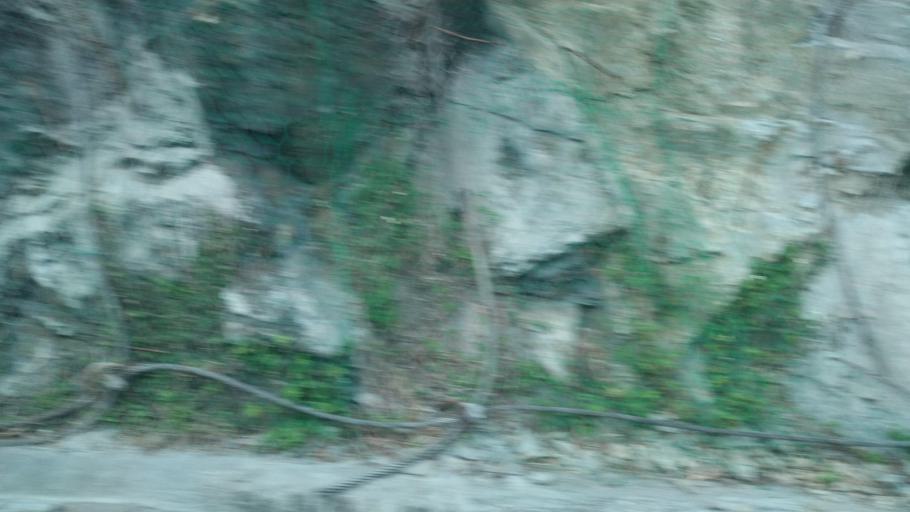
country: TW
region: Taiwan
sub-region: Hualien
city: Hualian
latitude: 24.2301
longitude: 121.7068
